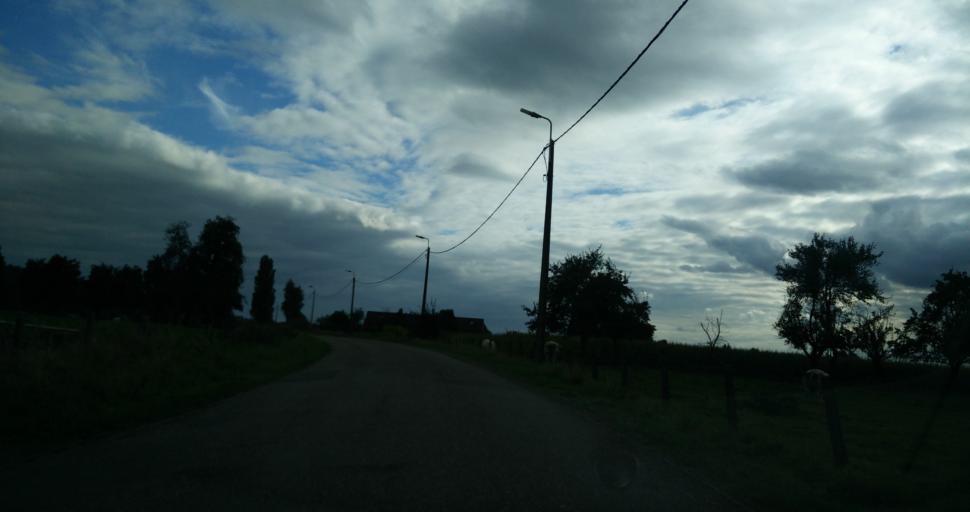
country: BE
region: Wallonia
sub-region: Province de Liege
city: Dalhem
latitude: 50.6964
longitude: 5.7167
